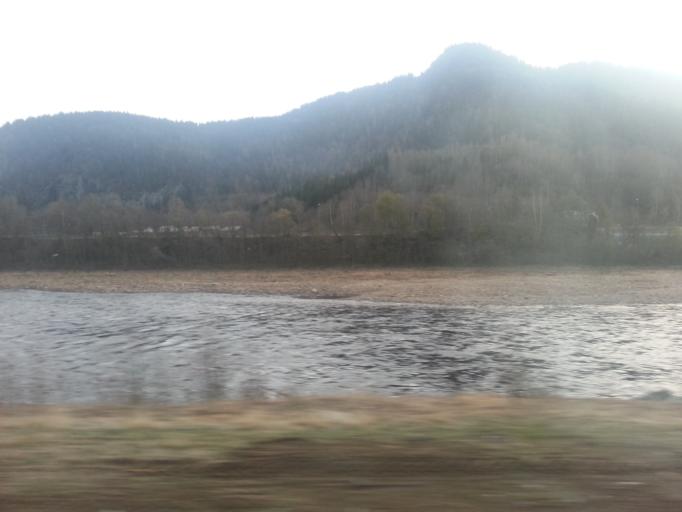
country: NO
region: Sor-Trondelag
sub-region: Midtre Gauldal
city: Storen
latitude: 63.0690
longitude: 10.2657
